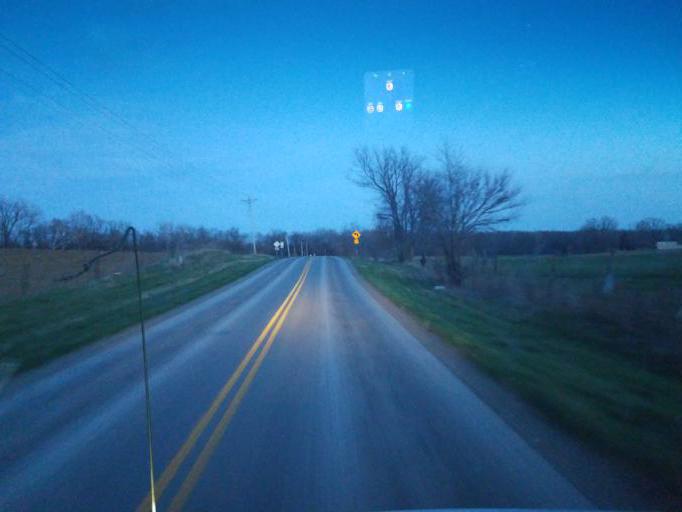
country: US
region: Ohio
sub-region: Logan County
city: De Graff
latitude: 40.3540
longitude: -83.9407
